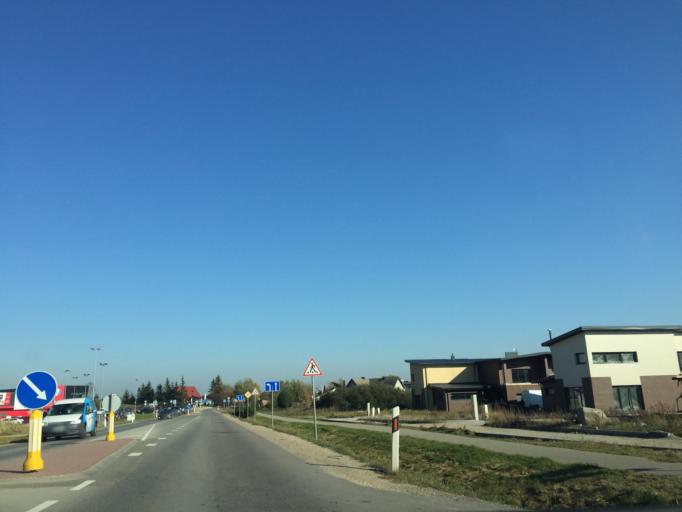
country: LT
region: Klaipedos apskritis
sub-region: Klaipeda
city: Klaipeda
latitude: 55.7352
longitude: 21.1909
